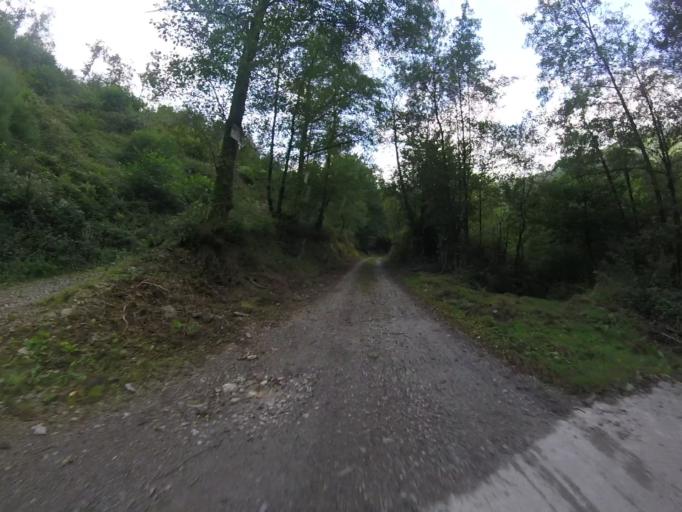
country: ES
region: Basque Country
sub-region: Provincia de Guipuzcoa
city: Berastegui
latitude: 43.1605
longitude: -1.9645
